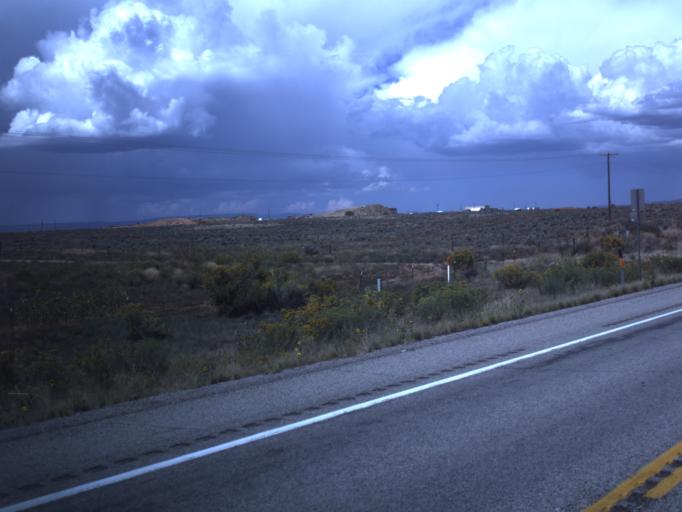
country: US
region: Utah
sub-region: San Juan County
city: Blanding
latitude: 37.5260
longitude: -109.4941
